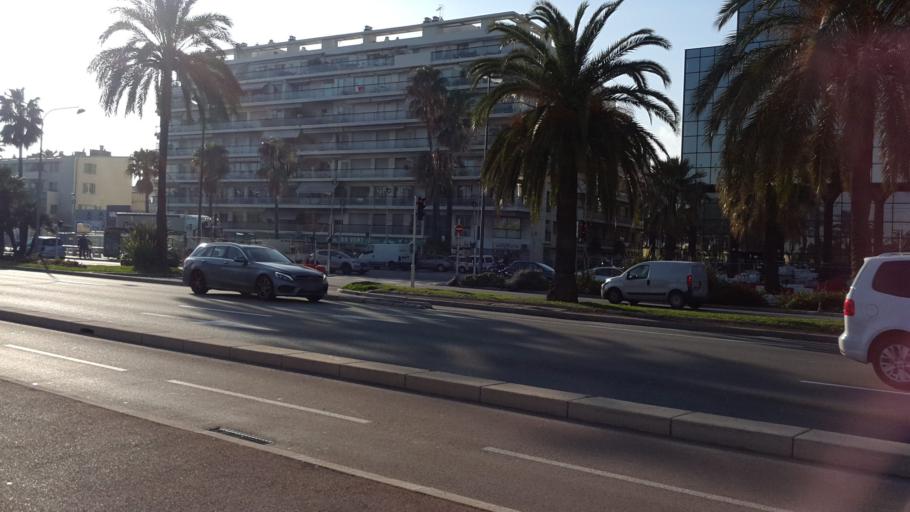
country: FR
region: Provence-Alpes-Cote d'Azur
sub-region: Departement des Alpes-Maritimes
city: Nice
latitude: 43.6781
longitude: 7.2297
